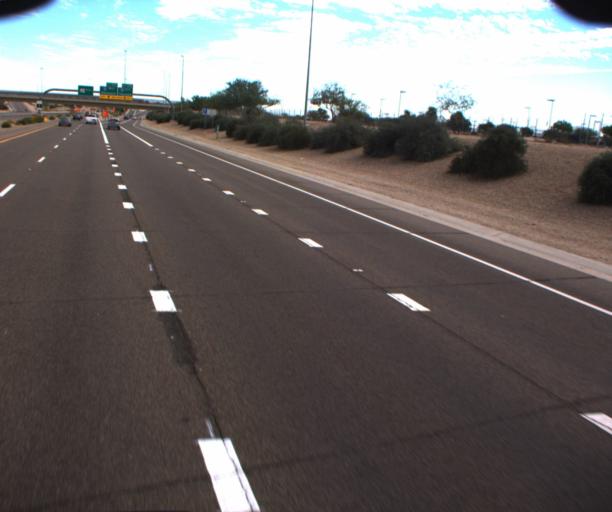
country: US
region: Arizona
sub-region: Maricopa County
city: Guadalupe
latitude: 33.2931
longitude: -111.9840
